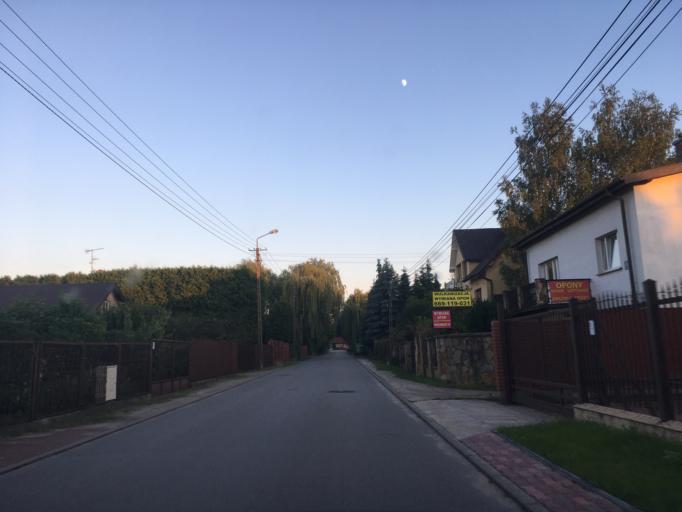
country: PL
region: Masovian Voivodeship
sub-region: Powiat piaseczynski
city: Piaseczno
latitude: 52.0669
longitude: 21.0113
